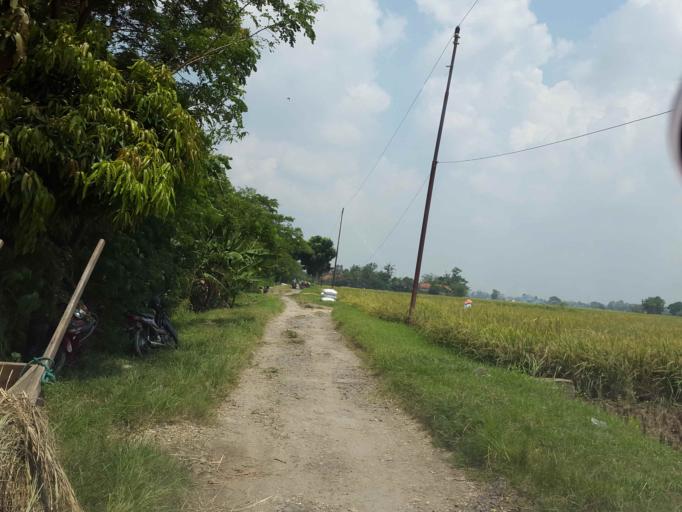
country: ID
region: Central Java
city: Dukuhkopi
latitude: -6.9612
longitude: 108.8253
